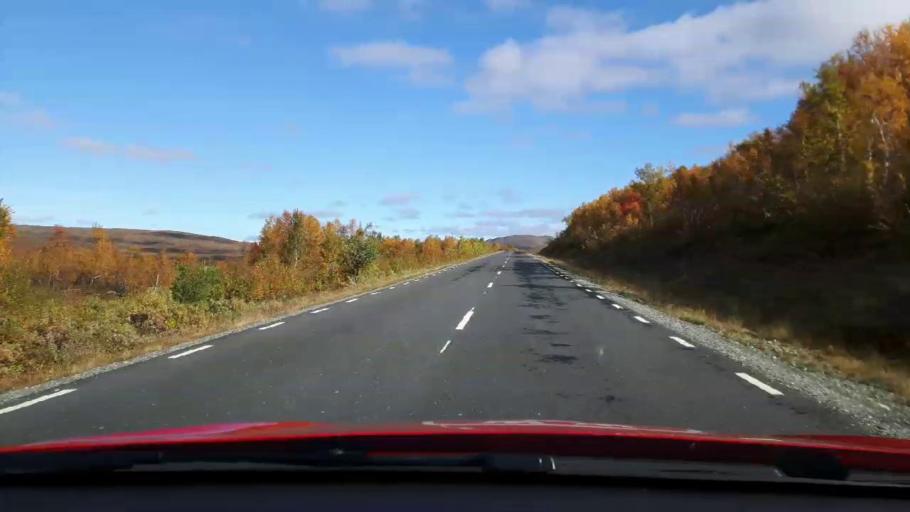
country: NO
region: Nordland
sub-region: Hattfjelldal
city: Hattfjelldal
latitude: 65.0033
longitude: 14.2528
